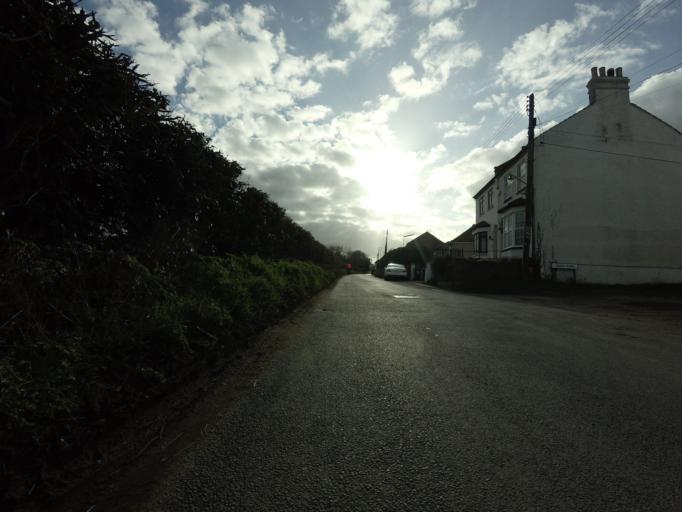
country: GB
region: England
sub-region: Kent
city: Dartford
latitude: 51.4216
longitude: 0.2267
